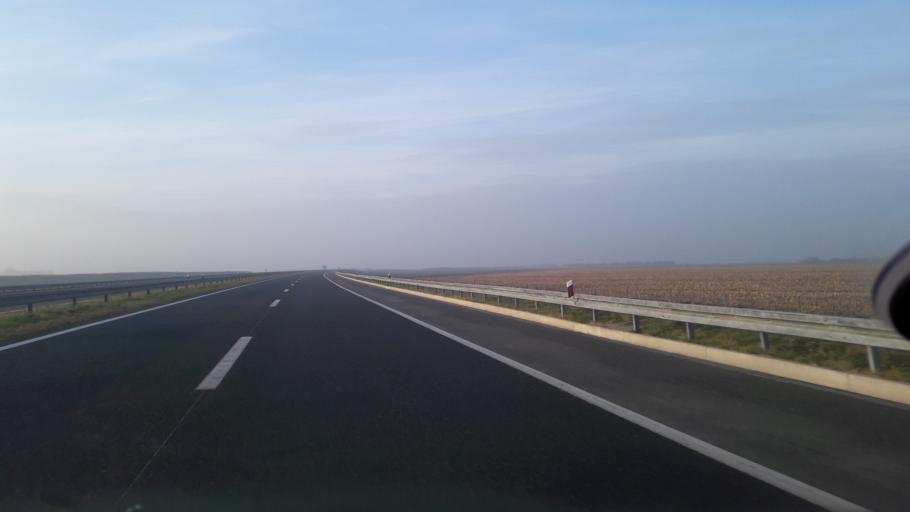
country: HR
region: Osjecko-Baranjska
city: Cepin
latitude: 45.5540
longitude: 18.5400
